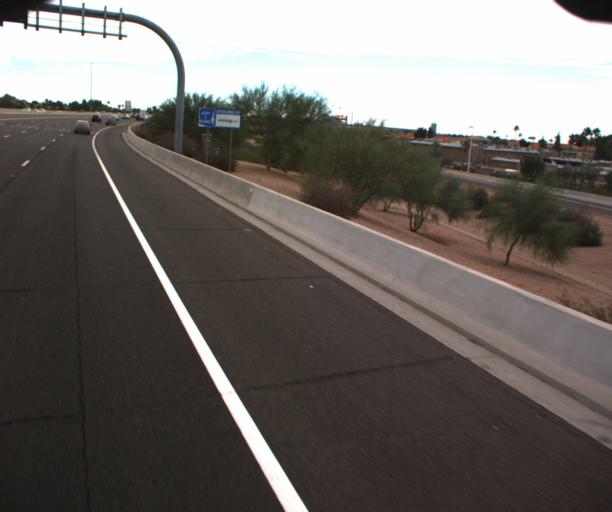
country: US
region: Arizona
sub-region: Maricopa County
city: Tempe Junction
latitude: 33.4557
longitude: -111.9742
